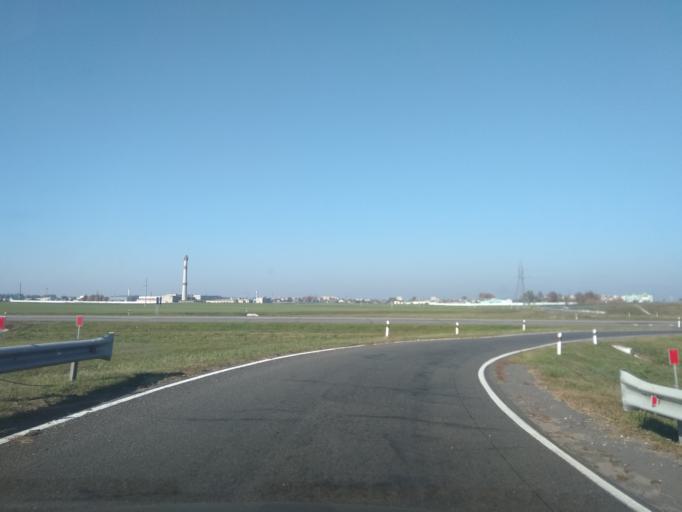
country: BY
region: Brest
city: Ivatsevichy
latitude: 52.6978
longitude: 25.3616
